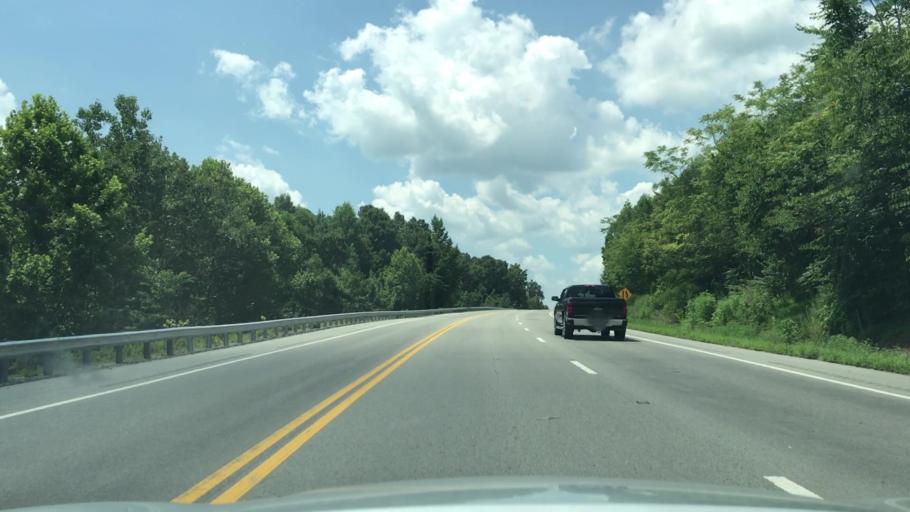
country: US
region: Tennessee
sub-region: Pickett County
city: Byrdstown
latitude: 36.5254
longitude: -85.1643
